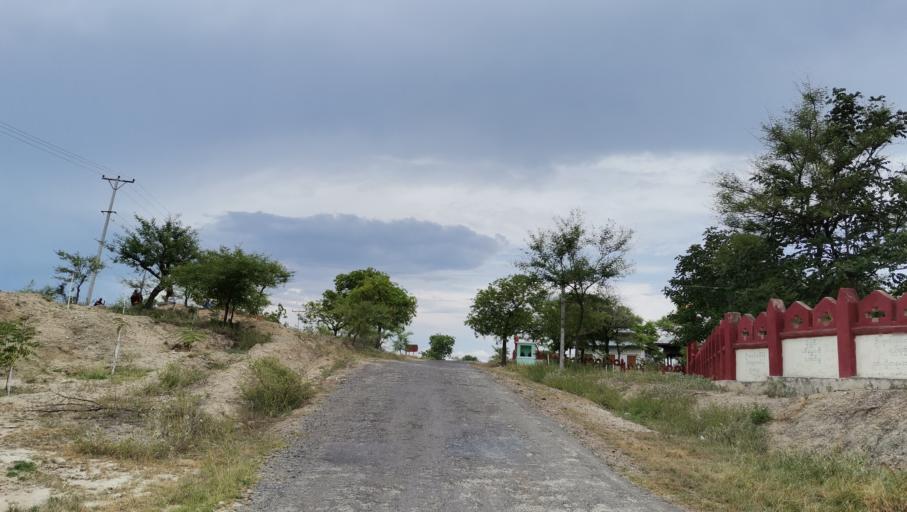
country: MM
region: Mandalay
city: Myingyan
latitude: 21.8191
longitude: 95.3973
